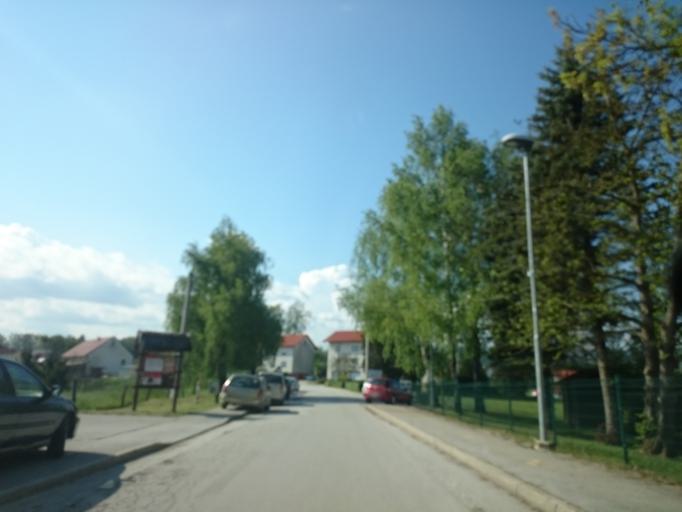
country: SI
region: Sentjur pri Celju
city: Sentjur
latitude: 46.2720
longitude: 15.3920
